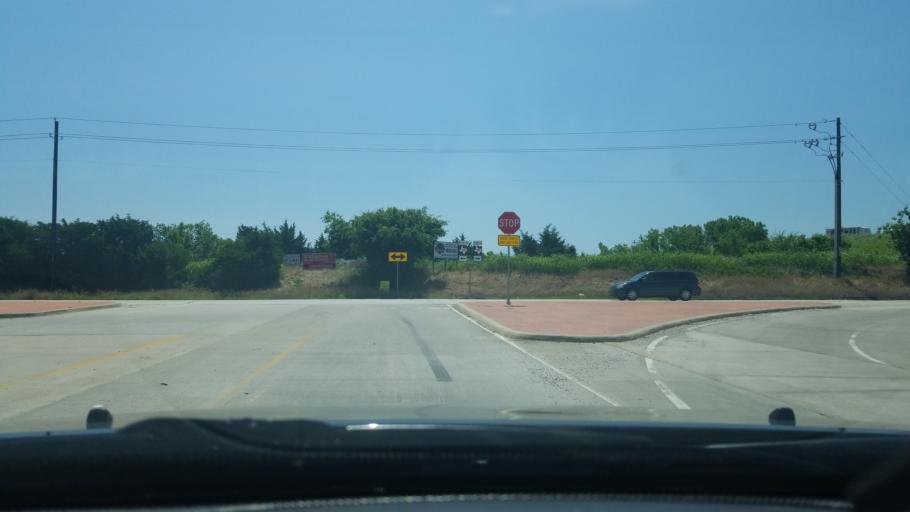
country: US
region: Texas
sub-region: Denton County
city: Krum
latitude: 33.2361
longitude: -97.2489
